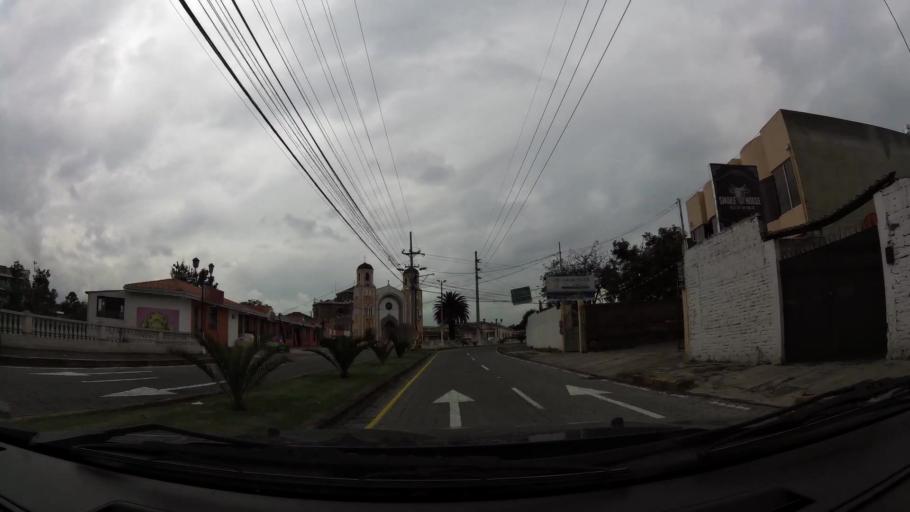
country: EC
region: Pichincha
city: Sangolqui
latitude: -0.3074
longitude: -78.4564
